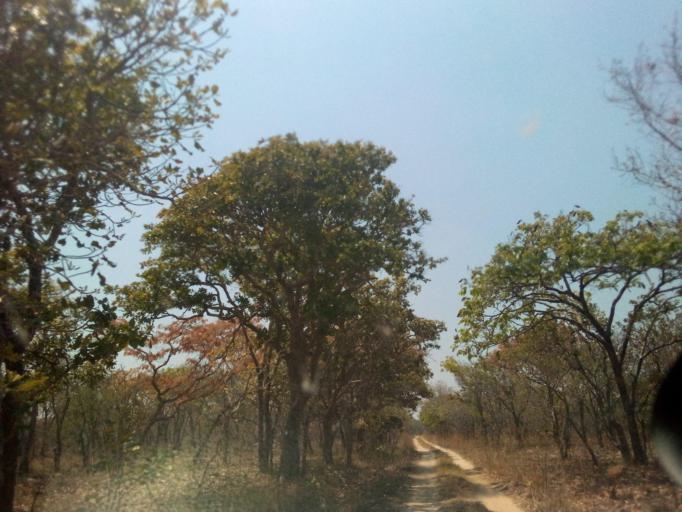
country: ZM
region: Copperbelt
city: Kataba
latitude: -12.2430
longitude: 30.3995
